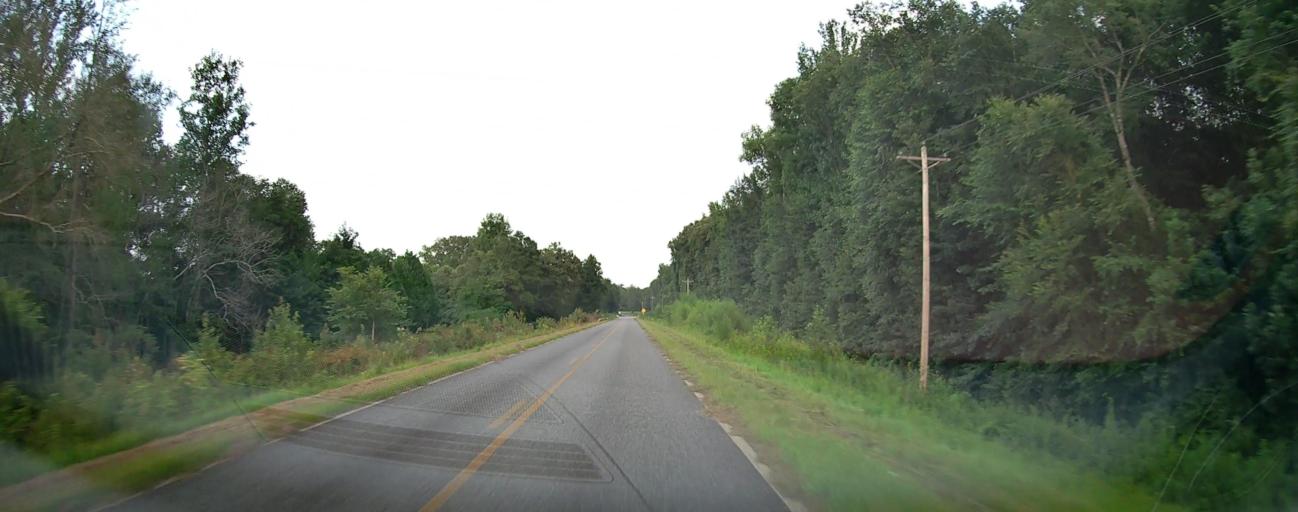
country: US
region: Georgia
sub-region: Crawford County
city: Roberta
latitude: 32.6531
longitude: -84.0360
